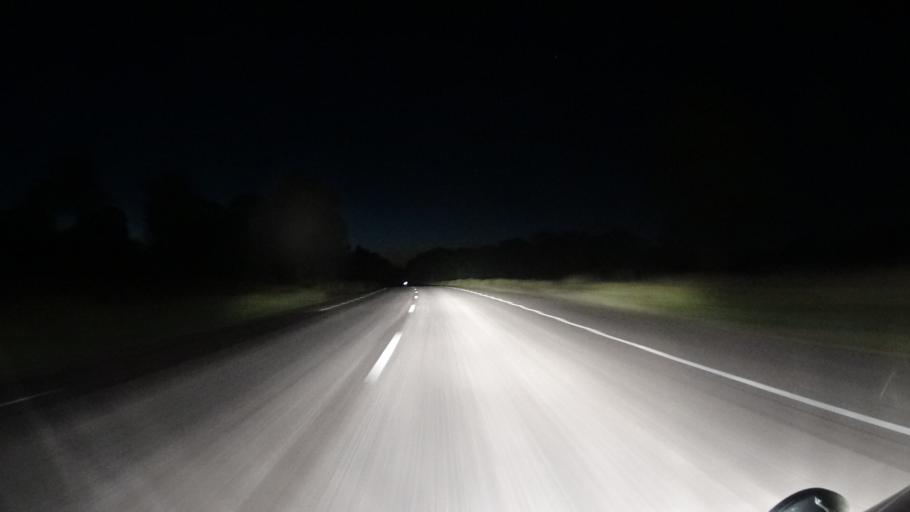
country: SE
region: OEstergoetland
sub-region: Odeshogs Kommun
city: OEdeshoeg
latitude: 58.2642
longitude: 14.7477
